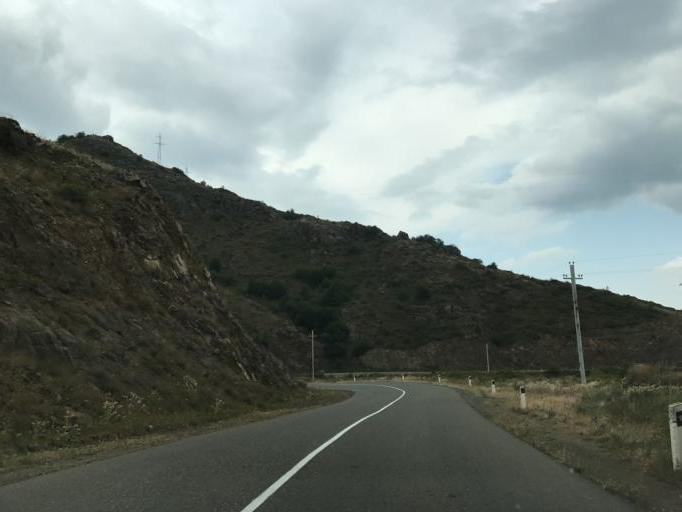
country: AZ
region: Susa
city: Shushi
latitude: 39.7195
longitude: 46.6828
